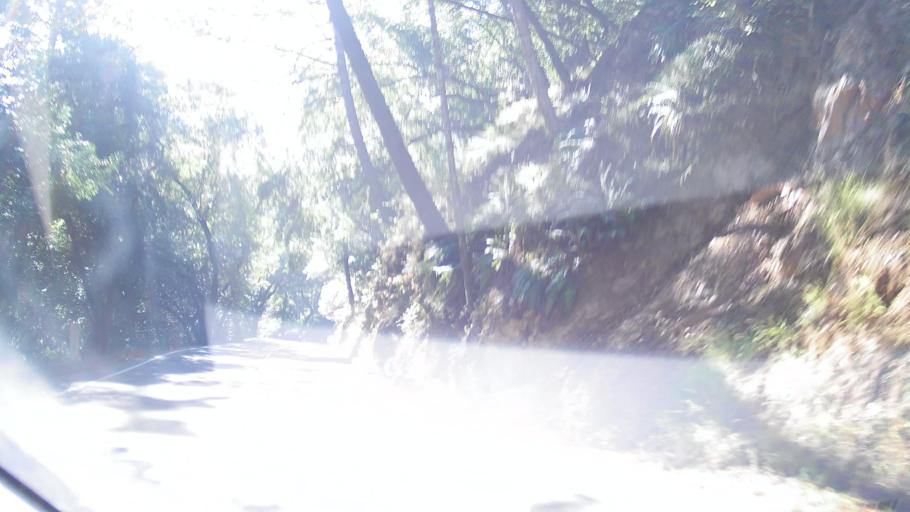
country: US
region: California
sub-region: Marin County
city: Mill Valley
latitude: 37.9047
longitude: -122.6105
